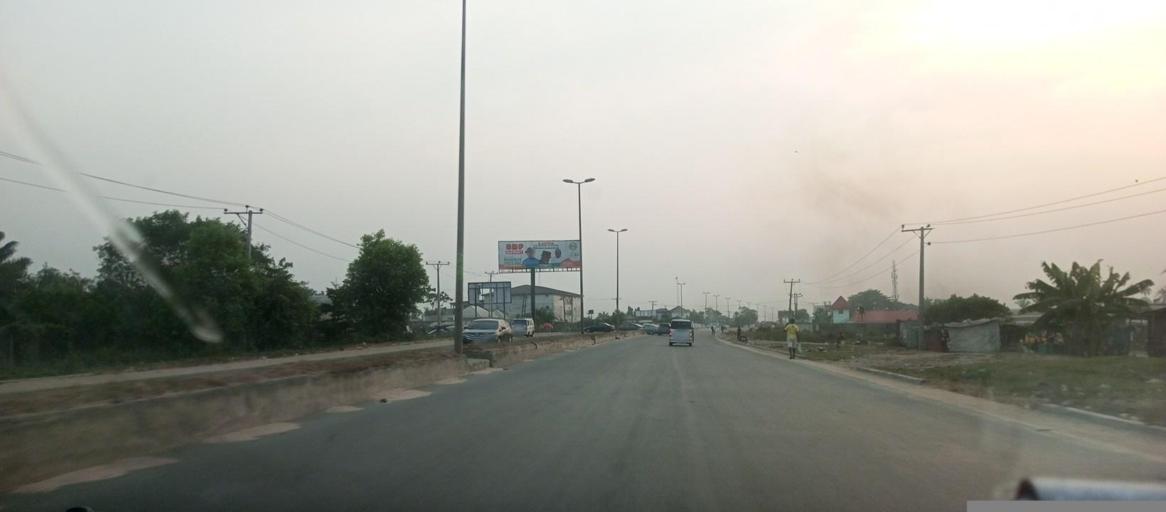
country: NG
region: Rivers
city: Emuoha
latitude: 4.9364
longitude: 7.0060
